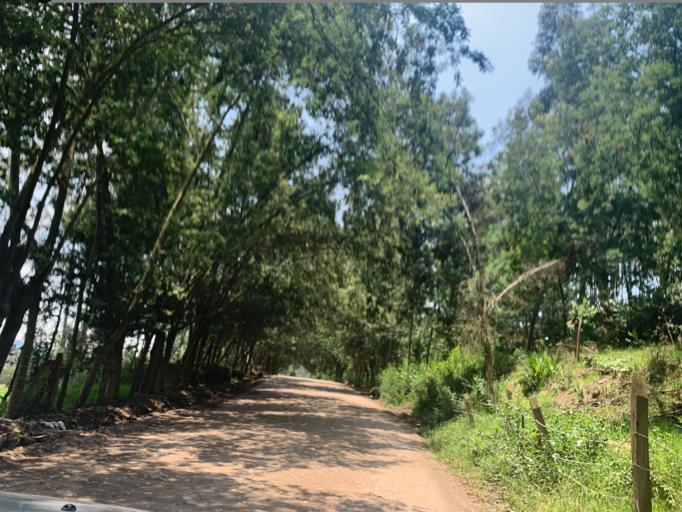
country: CO
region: Boyaca
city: Chiquinquira
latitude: 5.5871
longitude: -73.7475
